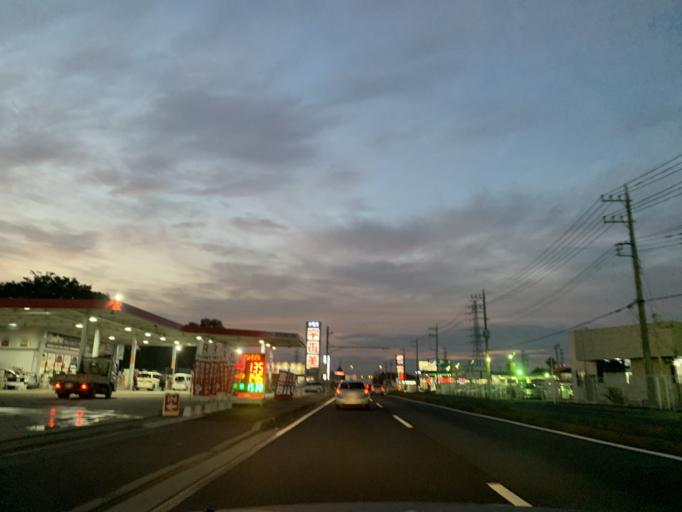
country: JP
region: Chiba
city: Noda
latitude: 35.9231
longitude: 139.9184
